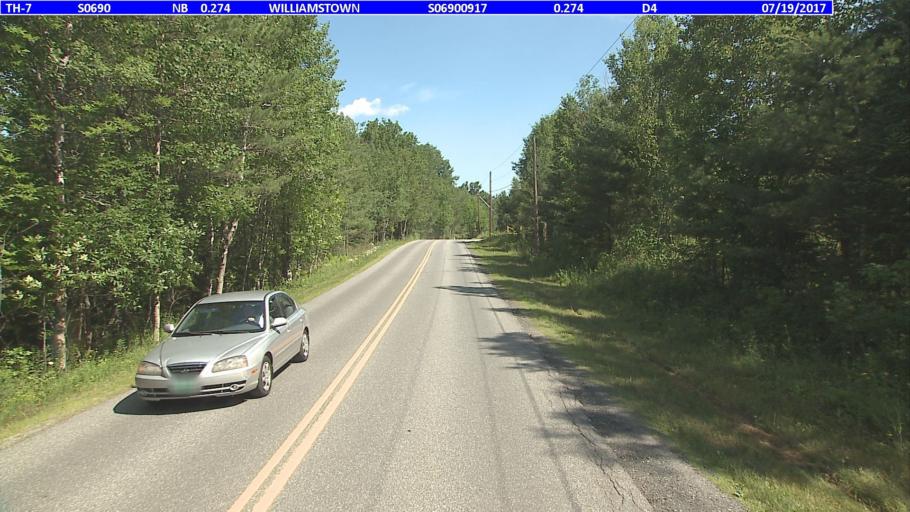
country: US
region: Vermont
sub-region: Washington County
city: South Barre
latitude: 44.1360
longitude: -72.4925
